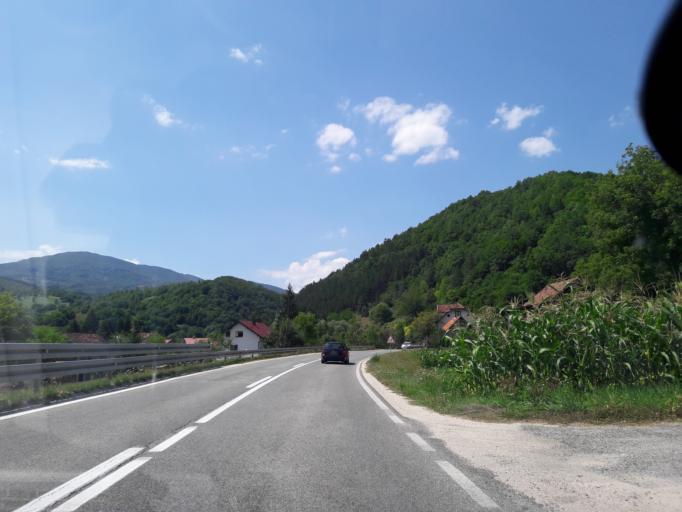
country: BA
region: Republika Srpska
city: Mrkonjic Grad
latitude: 44.3753
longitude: 17.1365
